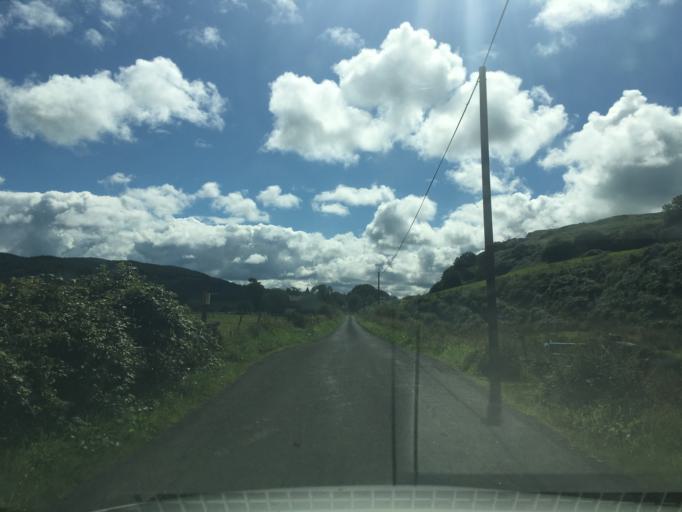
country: GB
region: Scotland
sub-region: Argyll and Bute
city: Lochgilphead
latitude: 56.0909
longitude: -5.4410
